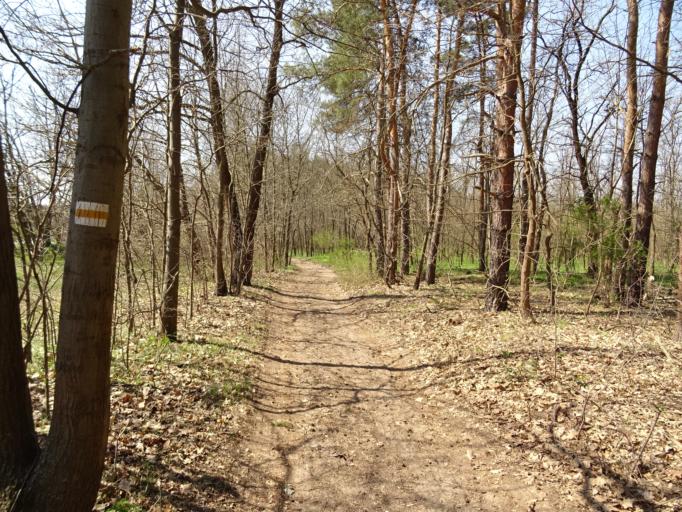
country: HU
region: Pest
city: Domony
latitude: 47.6266
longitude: 19.4167
